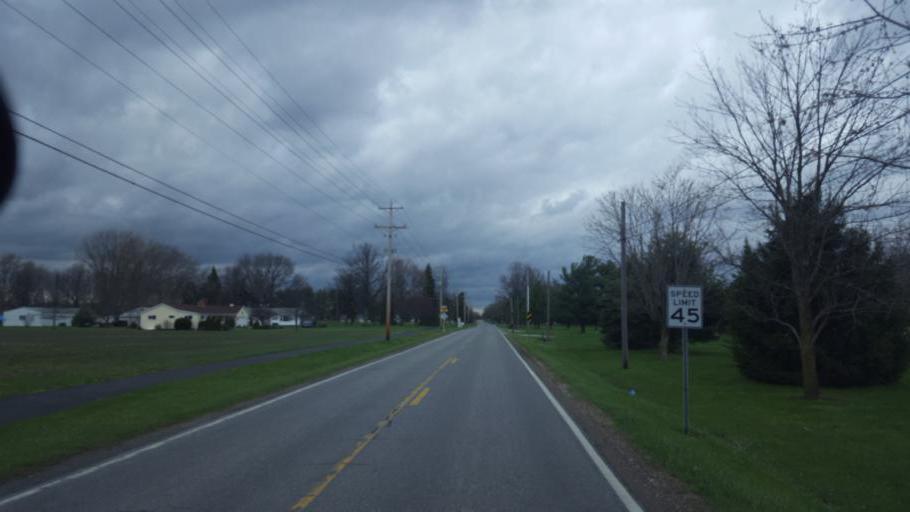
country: US
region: Ohio
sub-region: Franklin County
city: Westerville
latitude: 40.1798
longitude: -82.9027
